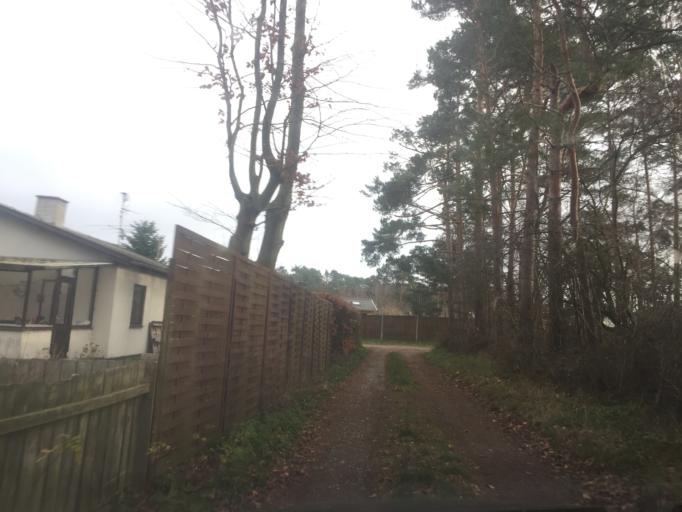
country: DK
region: Capital Region
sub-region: Halsnaes Kommune
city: Liseleje
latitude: 56.0077
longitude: 11.9933
